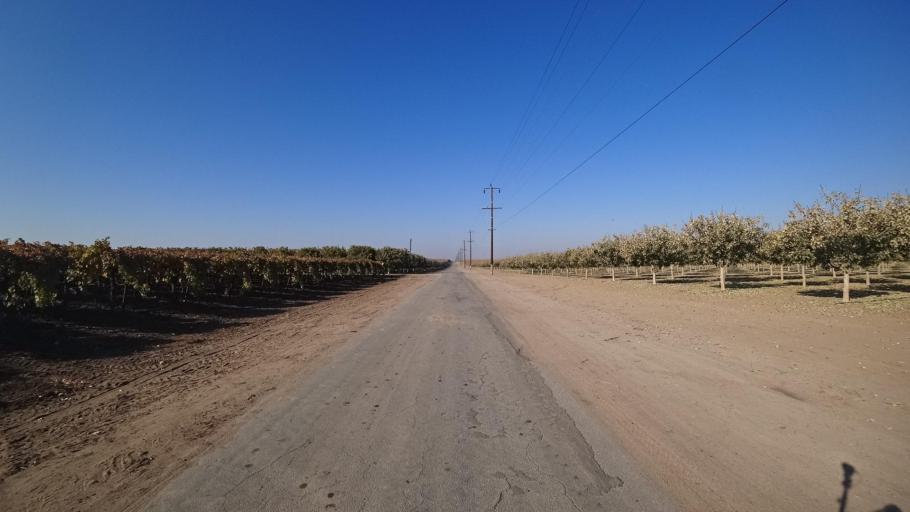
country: US
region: California
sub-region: Tulare County
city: Richgrove
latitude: 35.7327
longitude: -119.1067
